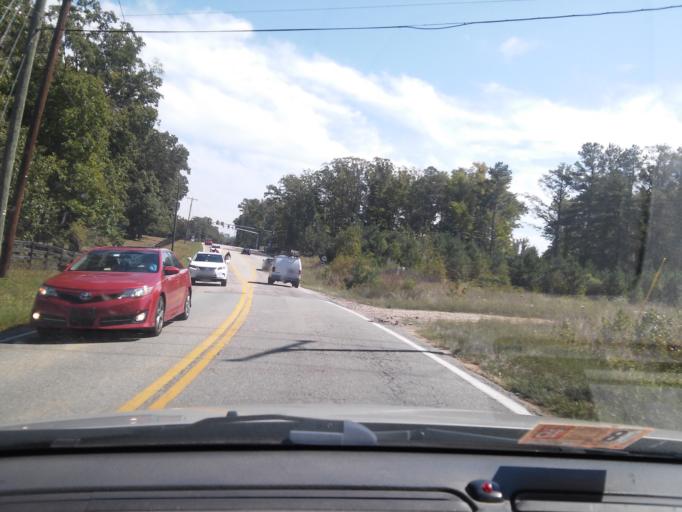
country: US
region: Virginia
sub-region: Henrico County
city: Short Pump
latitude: 37.5547
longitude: -77.6715
